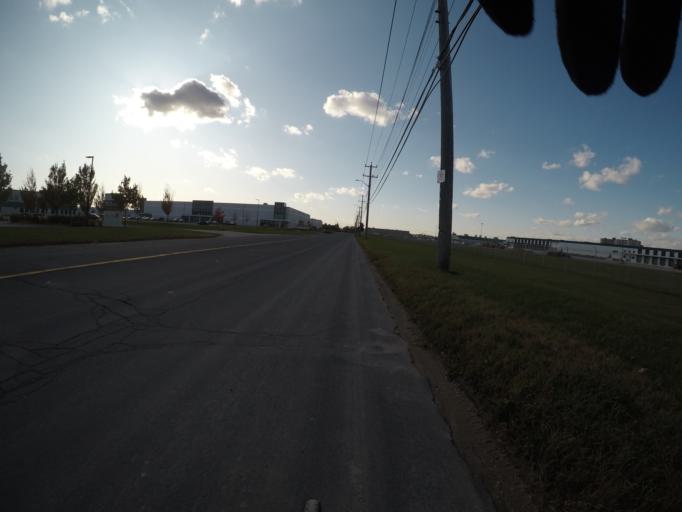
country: CA
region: Ontario
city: Kitchener
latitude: 43.4157
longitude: -80.4375
